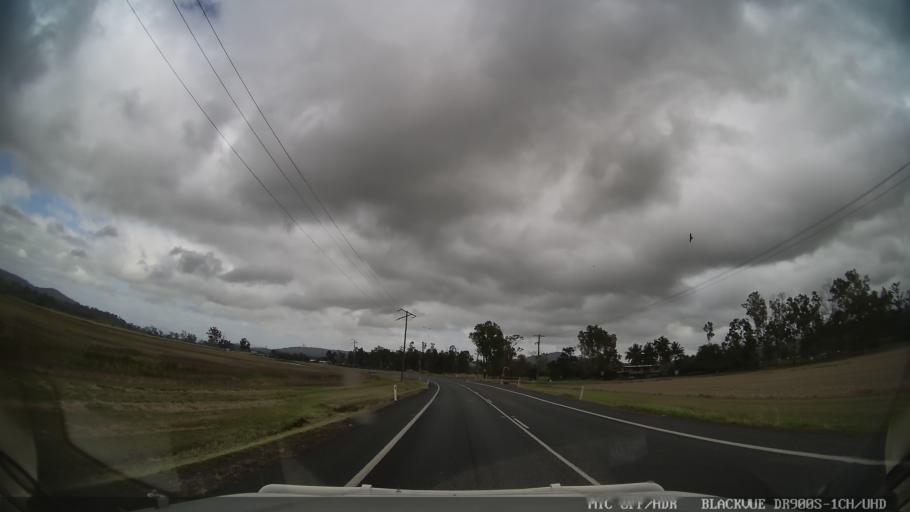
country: AU
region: Queensland
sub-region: Whitsunday
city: Proserpine
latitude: -20.3435
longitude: 148.6341
